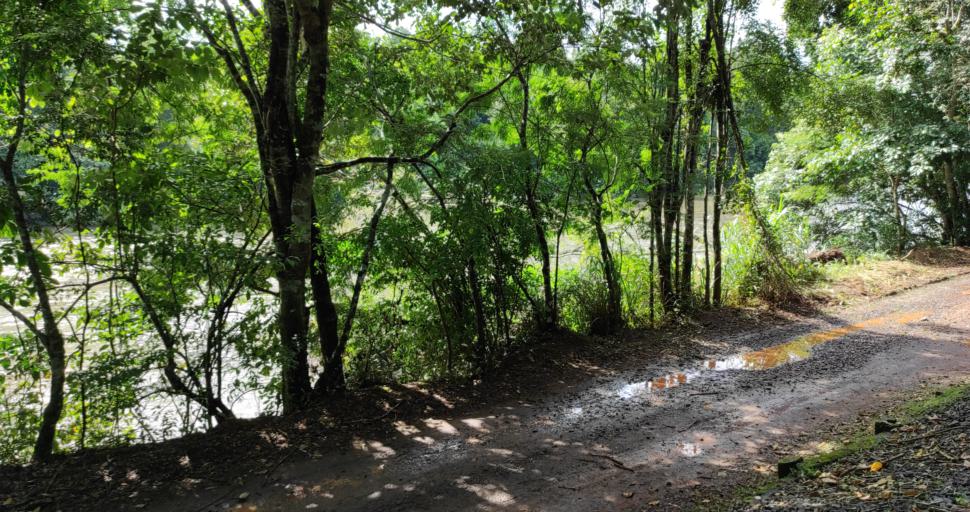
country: AR
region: Misiones
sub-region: Departamento de Iguazu
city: Puerto Iguazu
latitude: -25.6979
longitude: -54.4462
